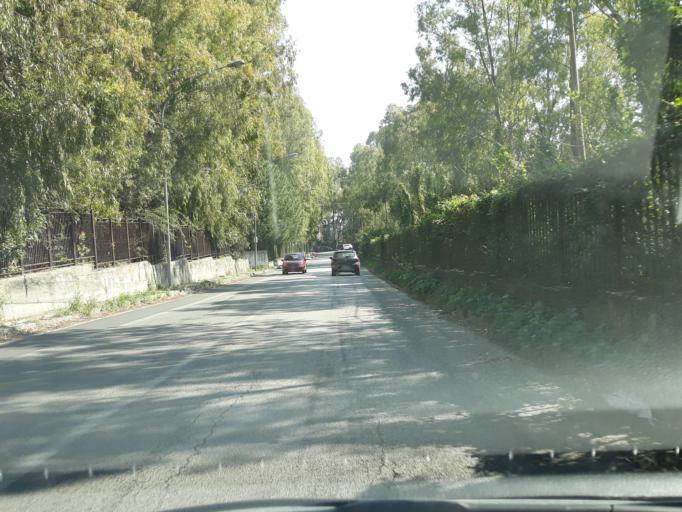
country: IT
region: Sicily
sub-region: Palermo
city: Palermo
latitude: 38.1196
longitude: 13.3035
